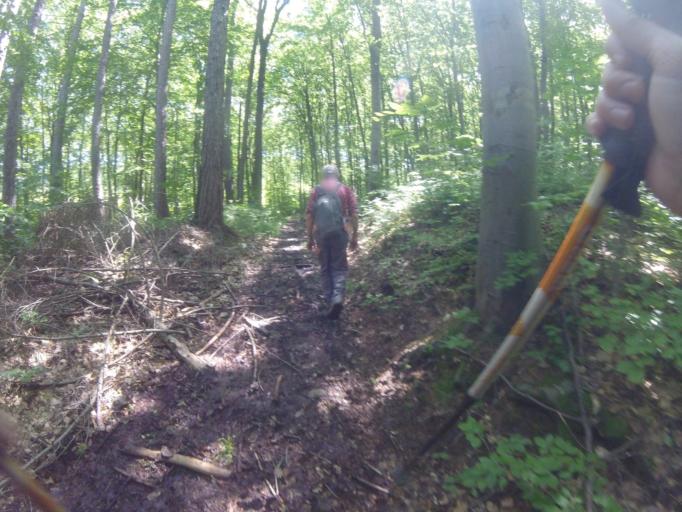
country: HU
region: Nograd
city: Batonyterenye
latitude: 47.9252
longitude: 19.8123
